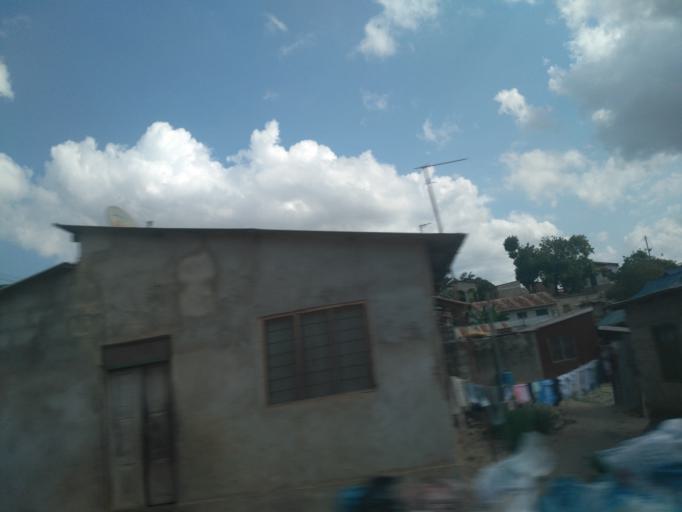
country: TZ
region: Dar es Salaam
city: Dar es Salaam
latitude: -6.8949
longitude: 39.2765
